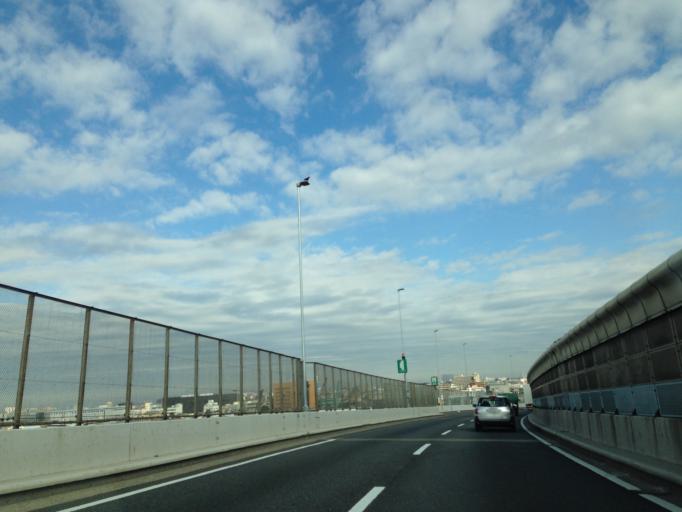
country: JP
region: Saitama
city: Kawaguchi
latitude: 35.7817
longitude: 139.7455
